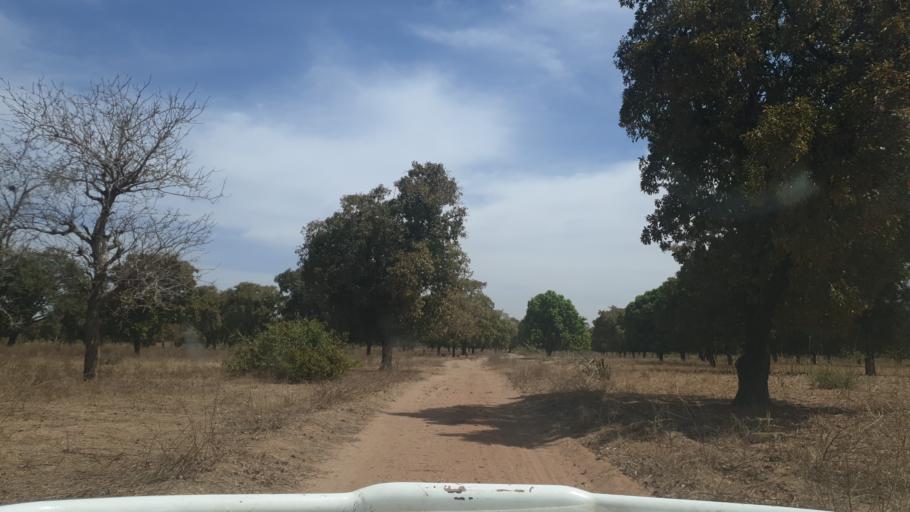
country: ML
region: Sikasso
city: Yorosso
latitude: 12.2916
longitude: -4.6668
